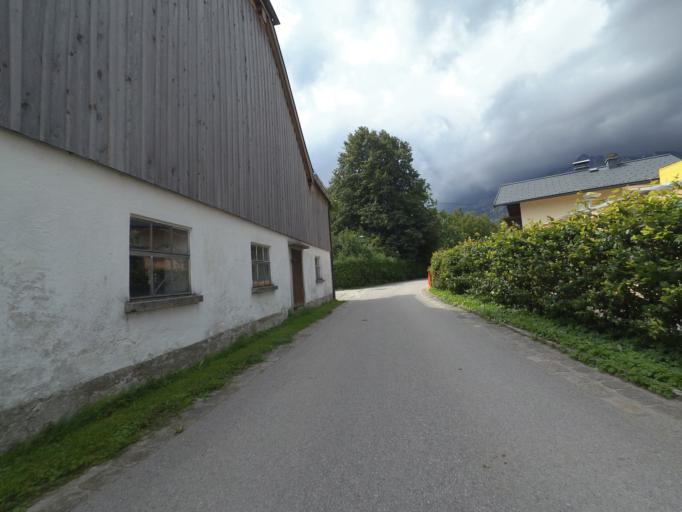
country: AT
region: Salzburg
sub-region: Politischer Bezirk Salzburg-Umgebung
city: Anif
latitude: 47.7300
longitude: 13.0645
